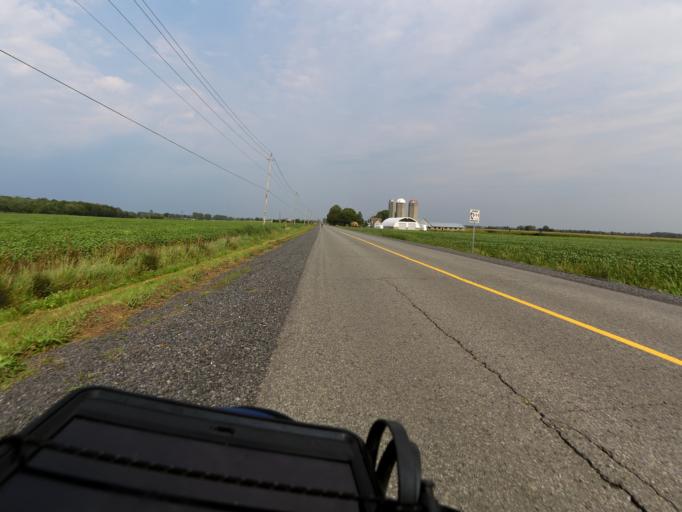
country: CA
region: Ontario
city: Casselman
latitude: 45.1842
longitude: -75.3479
